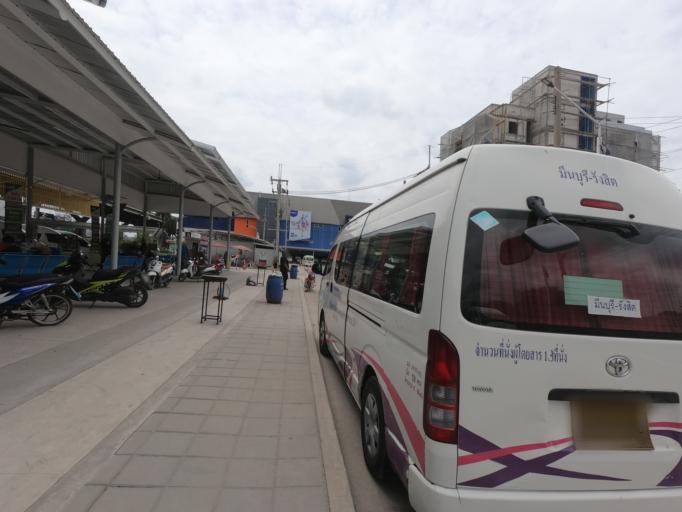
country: TH
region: Bangkok
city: Sai Mai
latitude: 13.9664
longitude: 100.6214
